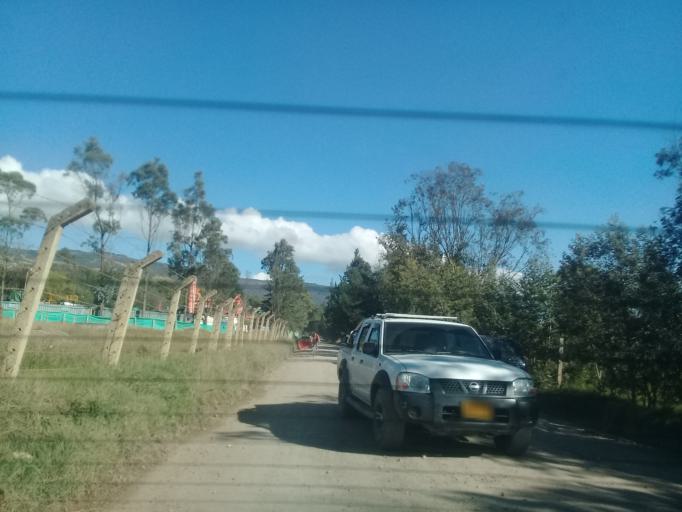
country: CO
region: Cundinamarca
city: Guasca
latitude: 4.8981
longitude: -73.8832
